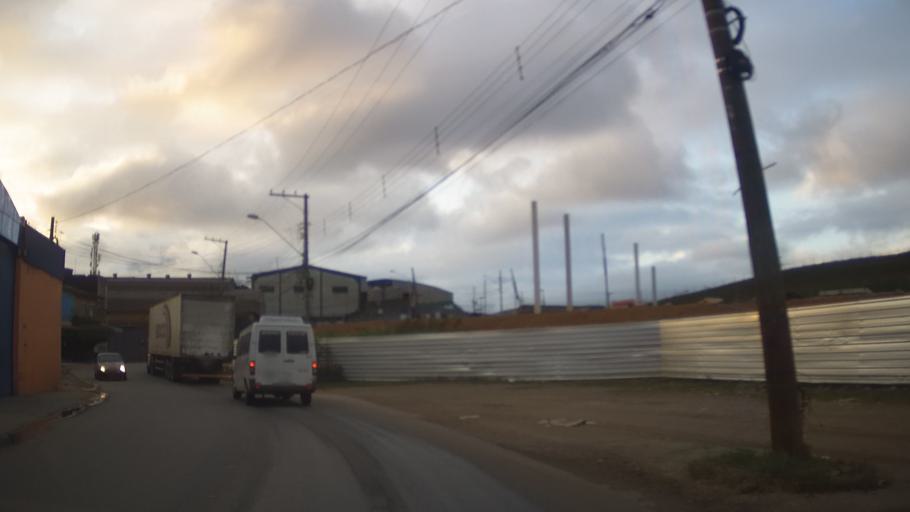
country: BR
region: Sao Paulo
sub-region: Itaquaquecetuba
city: Itaquaquecetuba
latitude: -23.4598
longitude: -46.4382
